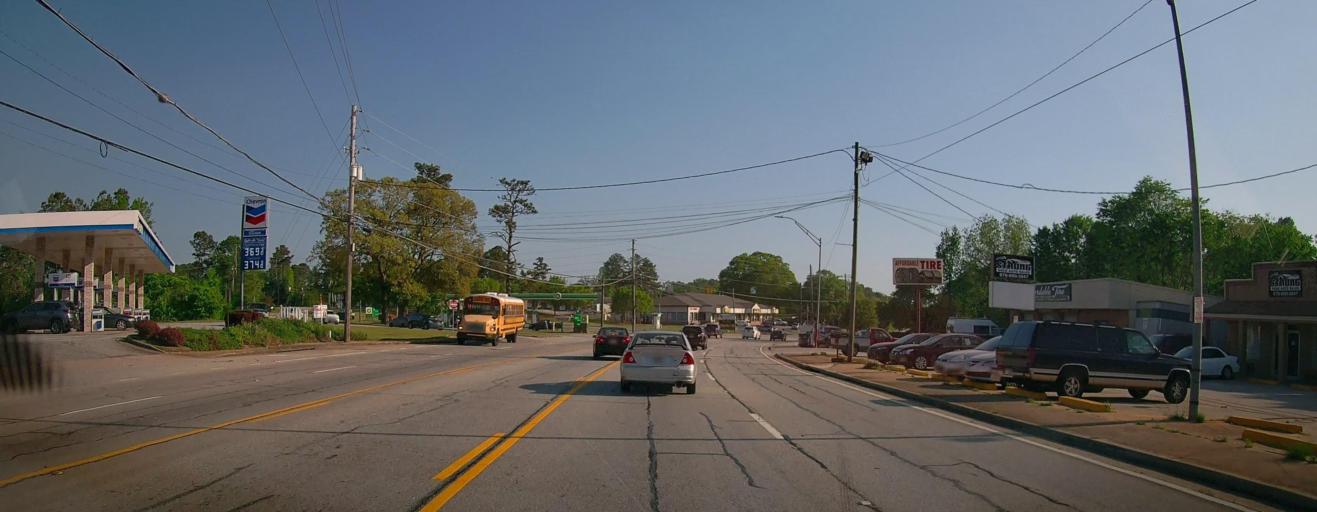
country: US
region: Georgia
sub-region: Newton County
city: Porterdale
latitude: 33.5850
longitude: -83.8775
